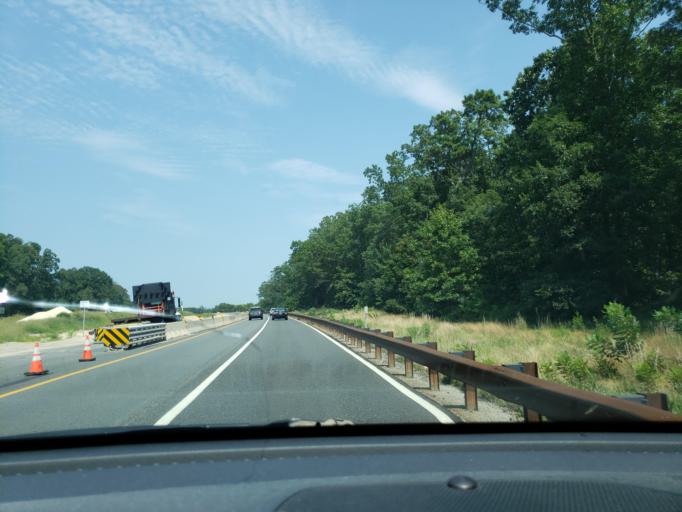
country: US
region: New Jersey
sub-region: Atlantic County
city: Linwood
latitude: 39.3449
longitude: -74.6004
